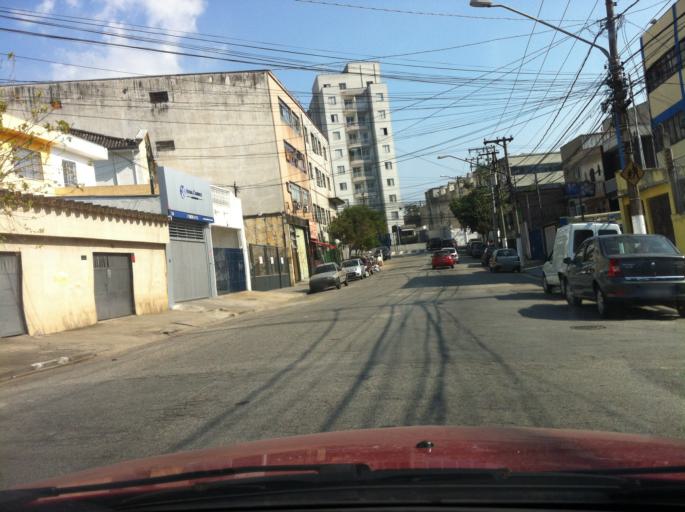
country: BR
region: Sao Paulo
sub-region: Diadema
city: Diadema
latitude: -23.6323
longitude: -46.6444
